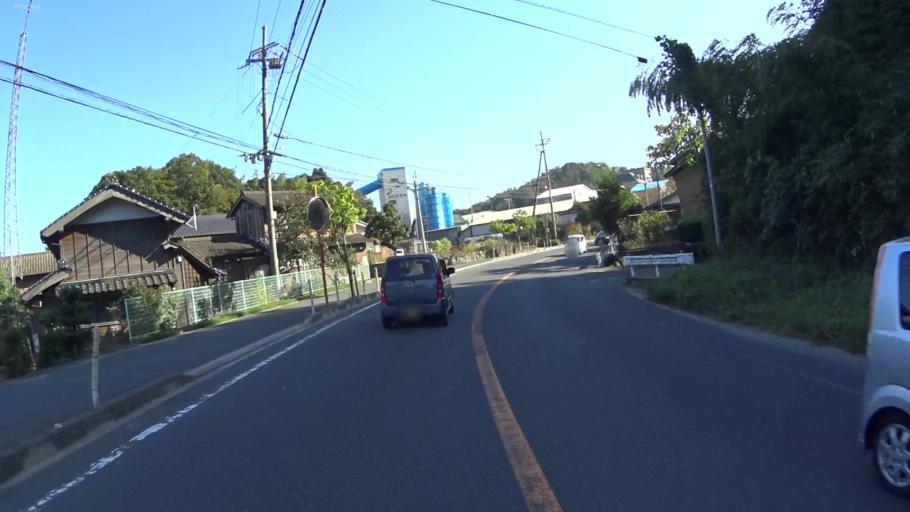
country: JP
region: Kyoto
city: Miyazu
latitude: 35.6389
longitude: 135.0541
